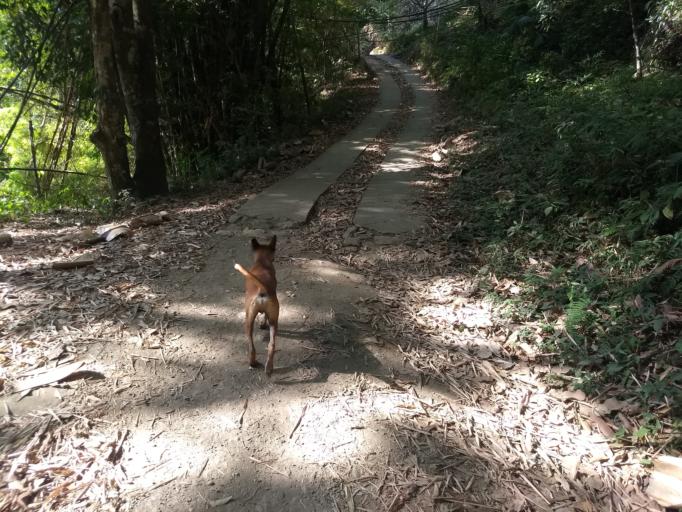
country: CO
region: Magdalena
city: Santa Marta
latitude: 11.1458
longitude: -74.1114
